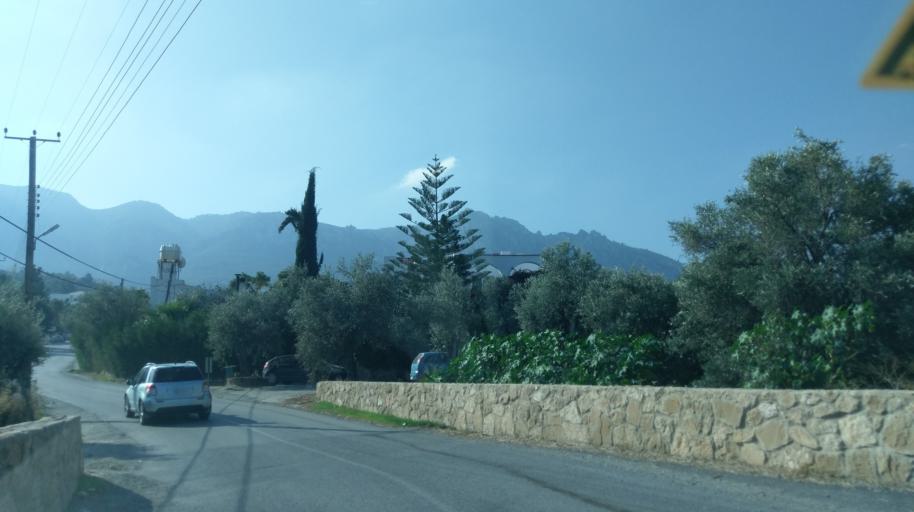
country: CY
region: Keryneia
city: Kyrenia
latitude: 35.3328
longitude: 33.2612
